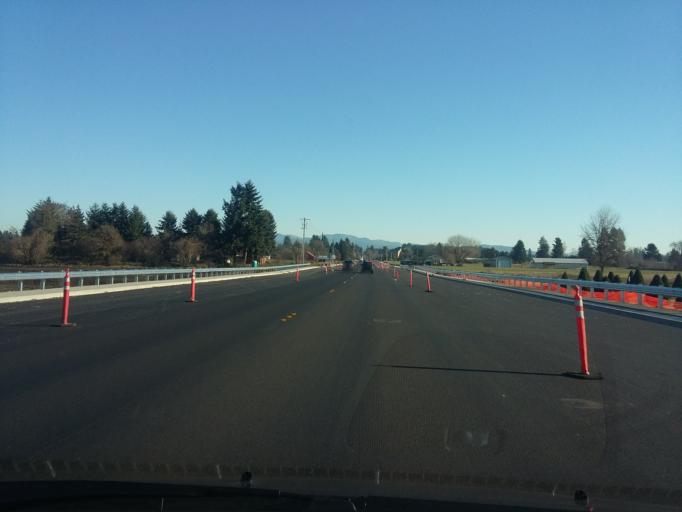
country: US
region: Washington
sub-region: Clark County
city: Barberton
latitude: 45.7077
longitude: -122.5913
